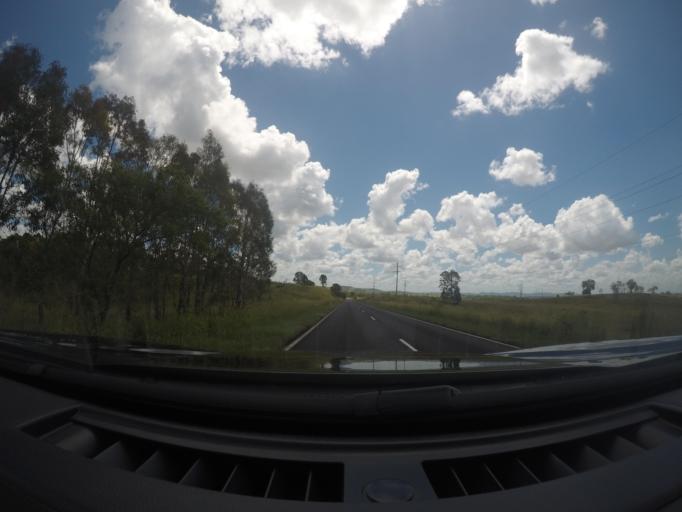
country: AU
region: Queensland
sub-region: Moreton Bay
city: Woodford
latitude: -27.1424
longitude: 152.4941
